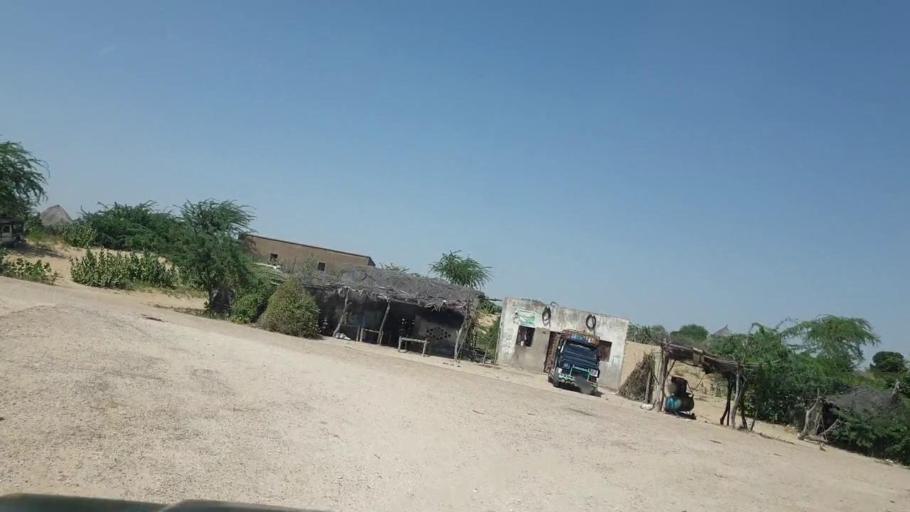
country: PK
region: Sindh
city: Chor
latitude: 25.4110
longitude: 70.3057
